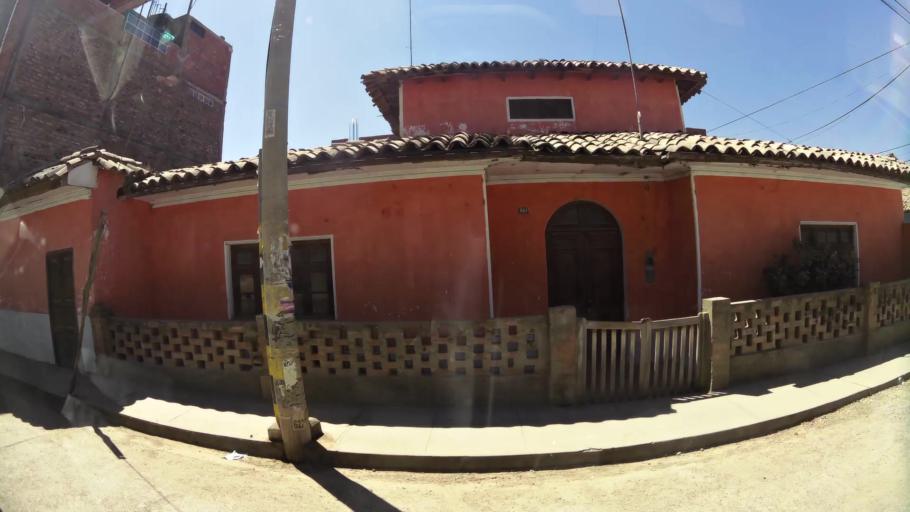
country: PE
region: Junin
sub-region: Provincia de Jauja
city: Jauja
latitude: -11.7733
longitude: -75.4960
